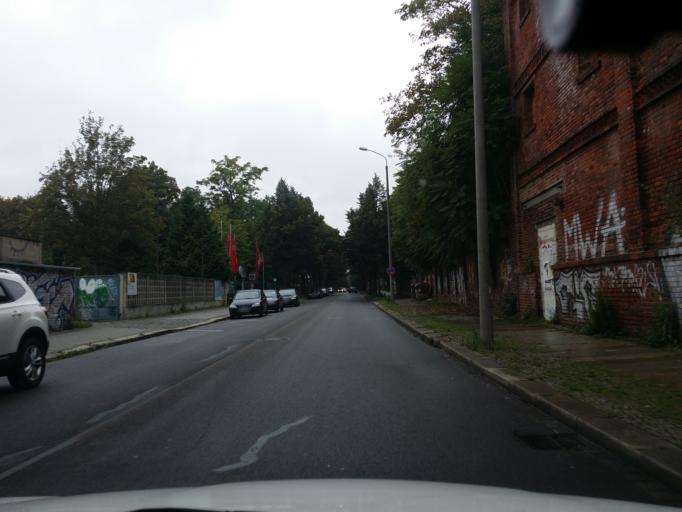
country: DE
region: Saxony
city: Leipzig
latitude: 51.3252
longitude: 12.3371
